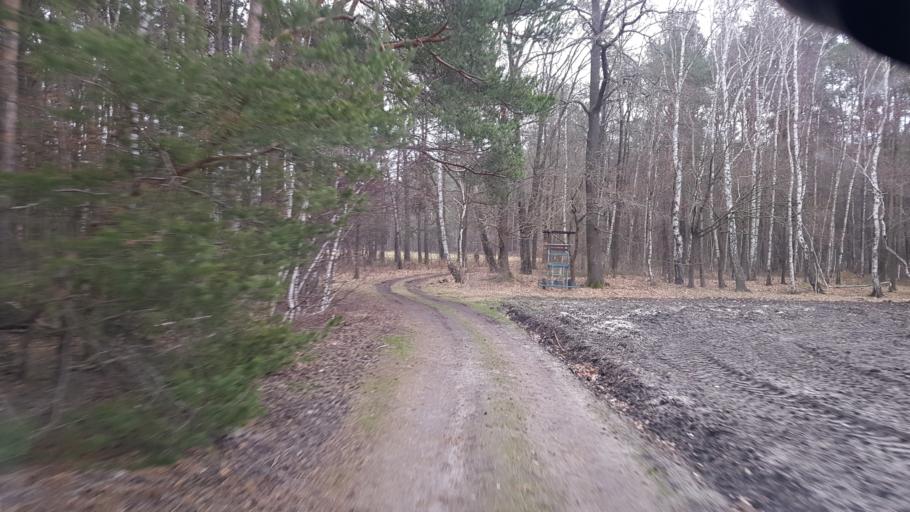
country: DE
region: Brandenburg
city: Schonborn
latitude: 51.6035
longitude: 13.5035
